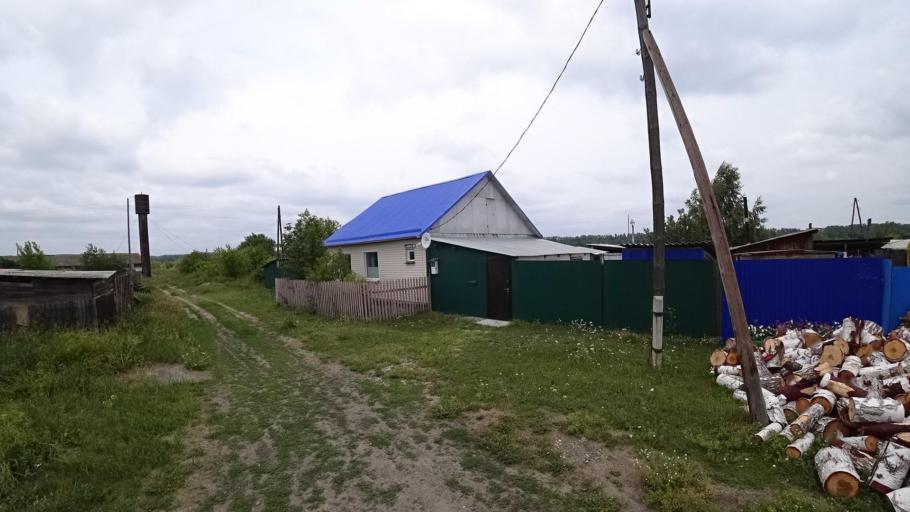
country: RU
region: Sverdlovsk
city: Kamyshlov
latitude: 56.8530
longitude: 62.6715
